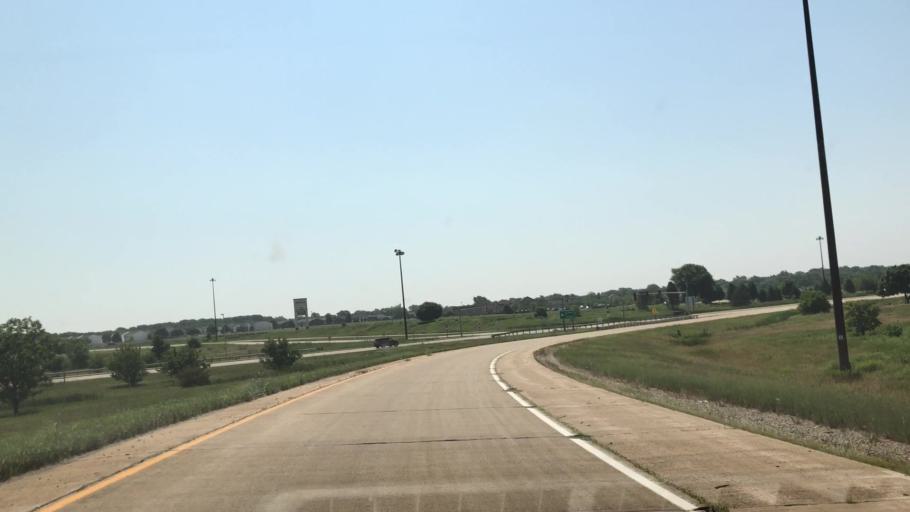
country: US
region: Illinois
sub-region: McLean County
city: Normal
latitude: 40.5382
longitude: -88.9980
